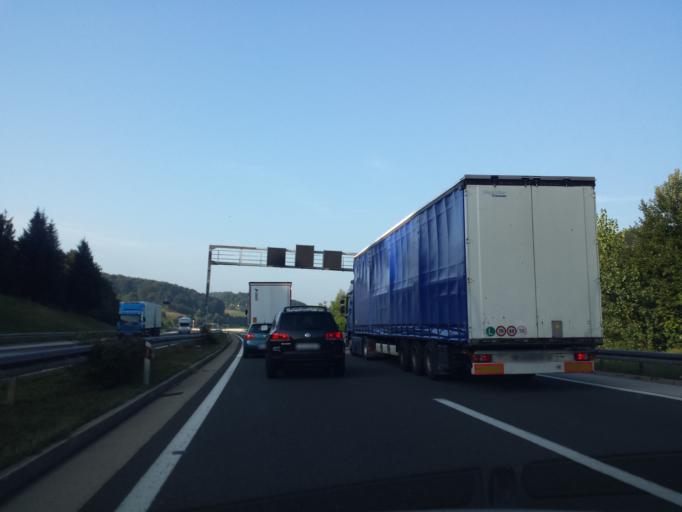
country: HR
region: Karlovacka
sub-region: Grad Karlovac
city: Karlovac
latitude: 45.4913
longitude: 15.4460
